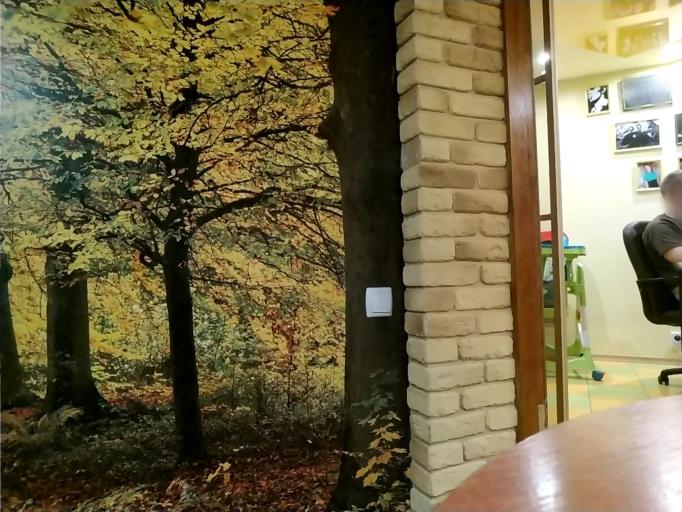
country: RU
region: Tverskaya
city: Zapadnaya Dvina
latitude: 56.3211
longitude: 31.9242
